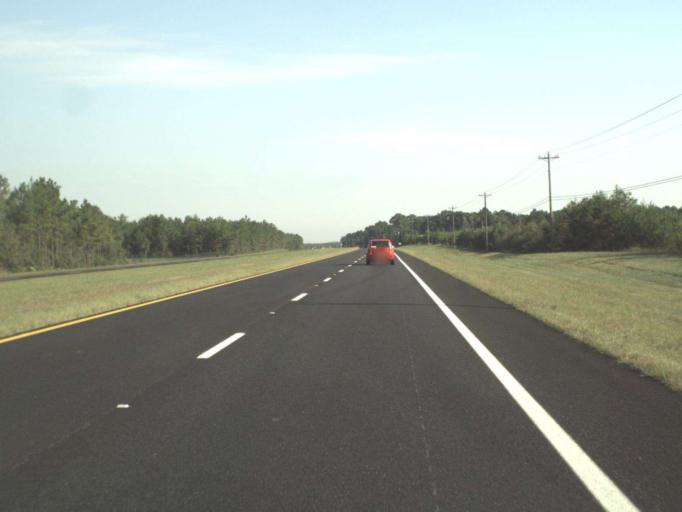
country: US
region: Florida
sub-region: Bay County
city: Laguna Beach
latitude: 30.4930
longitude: -85.8419
